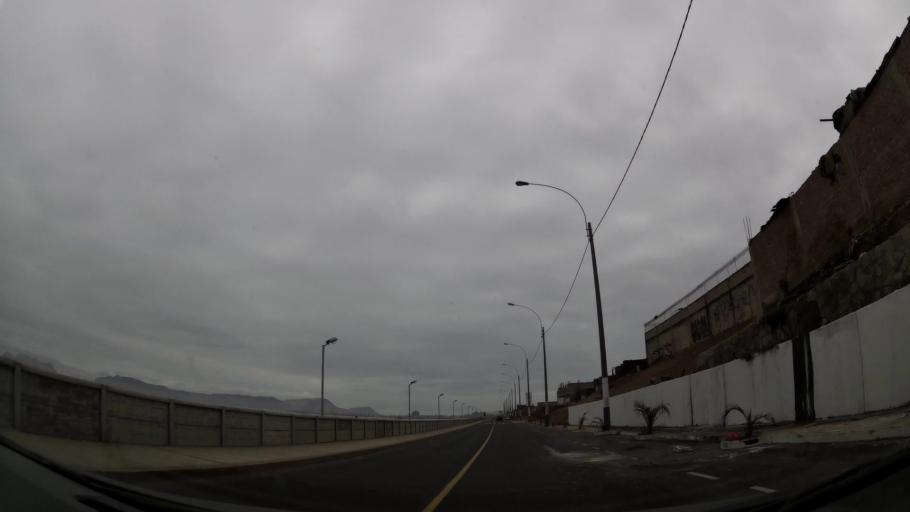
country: PE
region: Callao
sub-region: Callao
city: Callao
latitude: -12.0717
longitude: -77.1278
